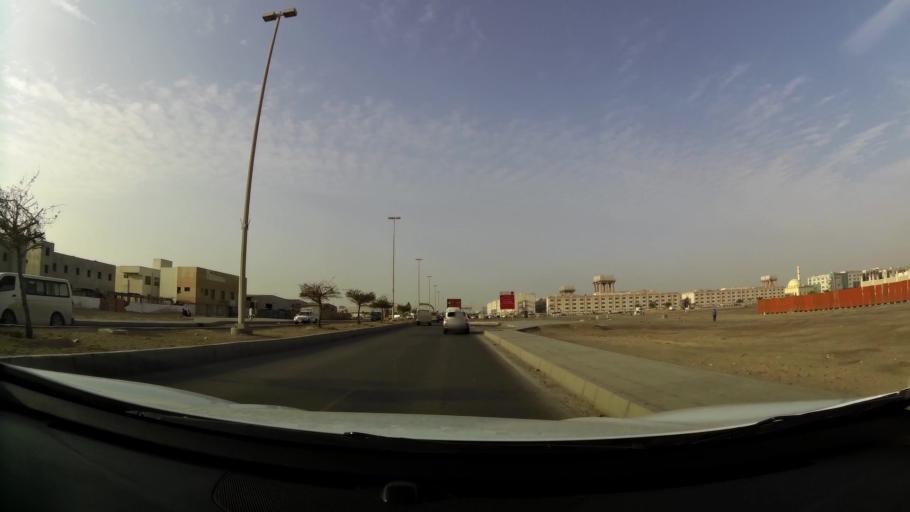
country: AE
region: Abu Dhabi
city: Abu Dhabi
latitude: 24.3575
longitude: 54.5168
